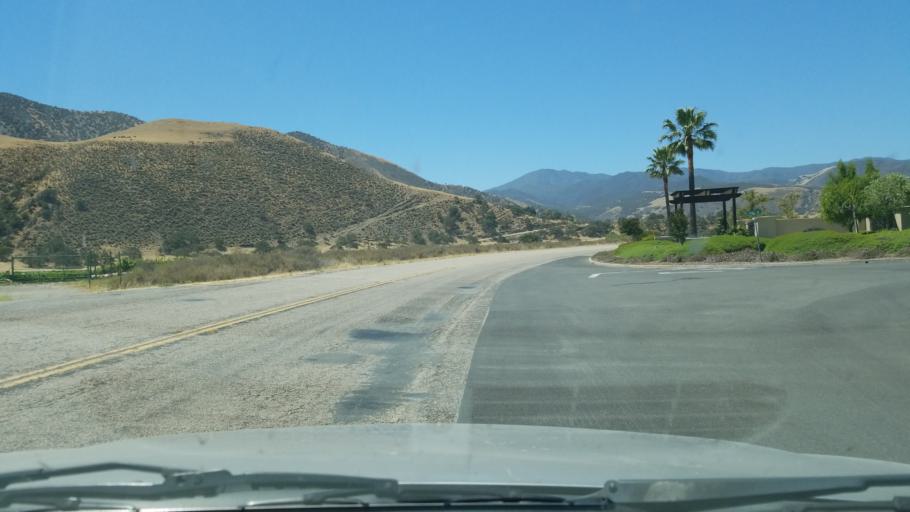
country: US
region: California
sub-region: Monterey County
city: Greenfield
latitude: 36.2827
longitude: -121.3209
